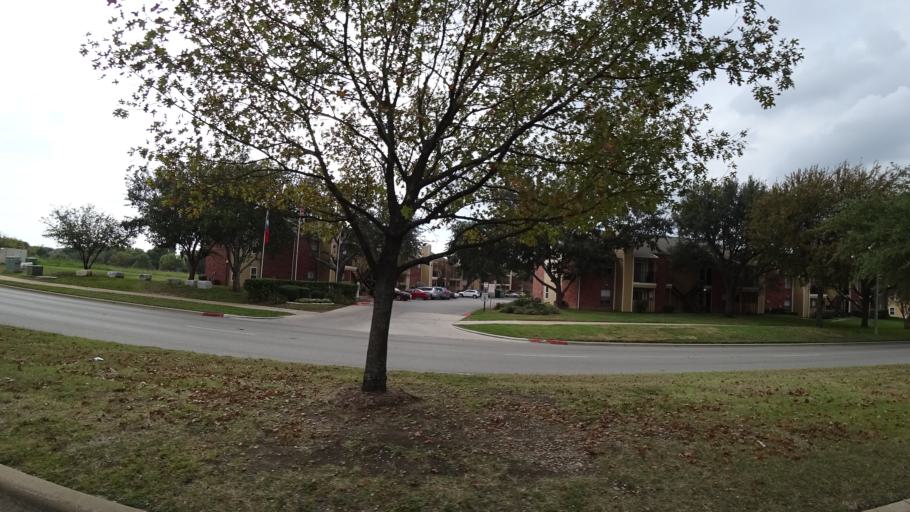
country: US
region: Texas
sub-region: Travis County
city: Wells Branch
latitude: 30.4395
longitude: -97.6858
